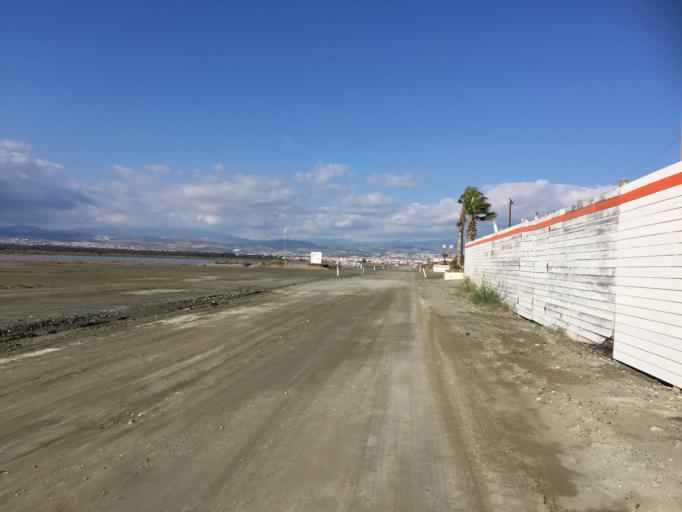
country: CY
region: Limassol
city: Limassol
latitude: 34.6204
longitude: 33.0054
